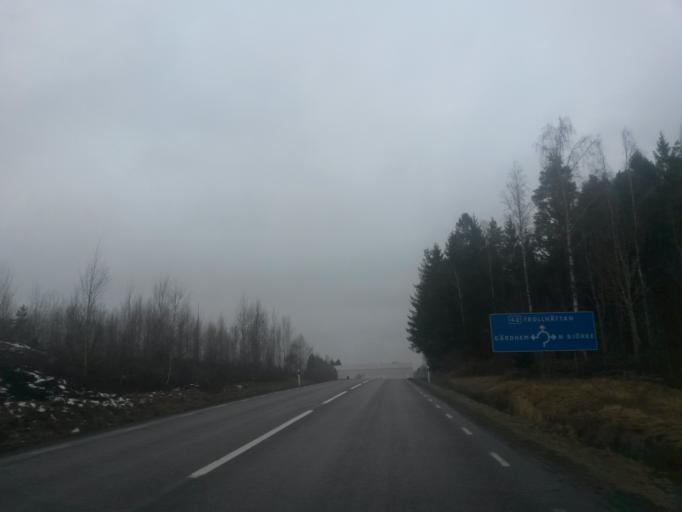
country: SE
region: Vaestra Goetaland
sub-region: Vanersborgs Kommun
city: Vargon
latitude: 58.2594
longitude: 12.4033
